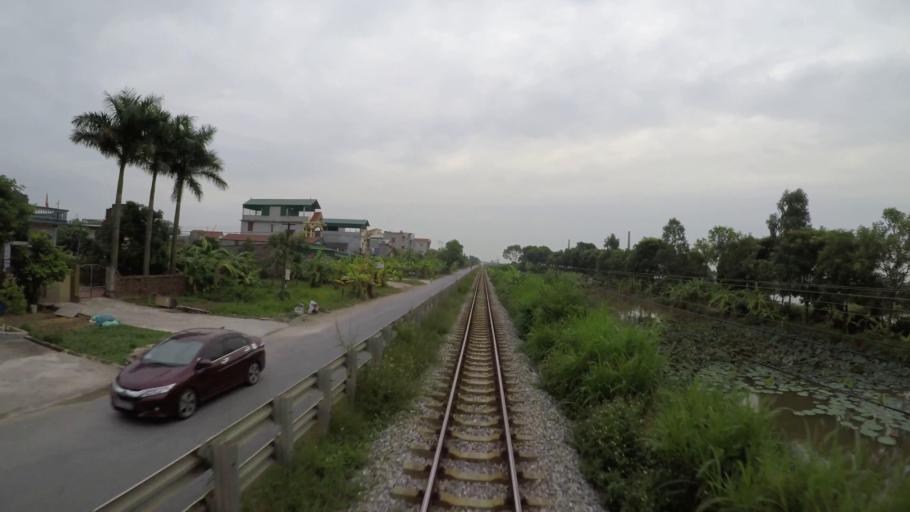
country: VN
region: Hung Yen
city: Ban Yen Nhan
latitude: 20.9653
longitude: 106.1144
